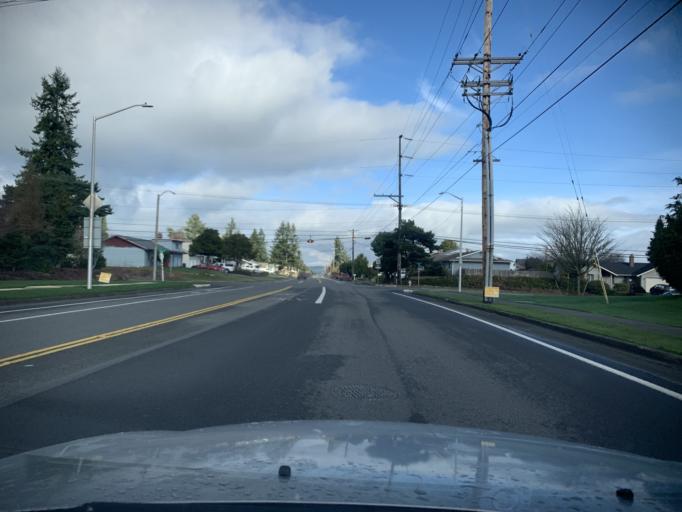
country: US
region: Washington
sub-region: Pierce County
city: Fircrest
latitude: 47.2818
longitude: -122.5212
